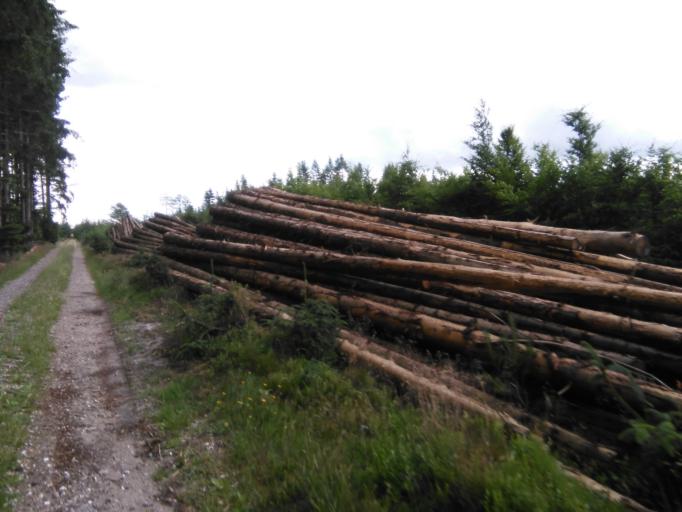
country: DK
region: Central Jutland
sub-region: Silkeborg Kommune
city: Virklund
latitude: 56.0776
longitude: 9.4651
